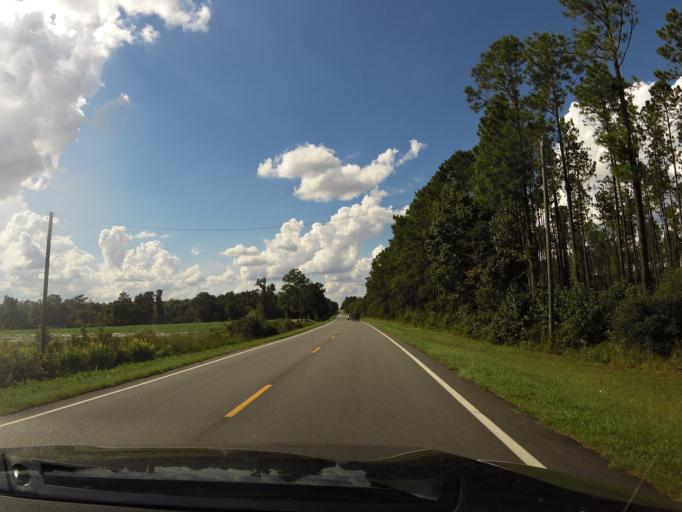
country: US
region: Georgia
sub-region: Echols County
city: Statenville
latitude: 30.7658
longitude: -83.1300
